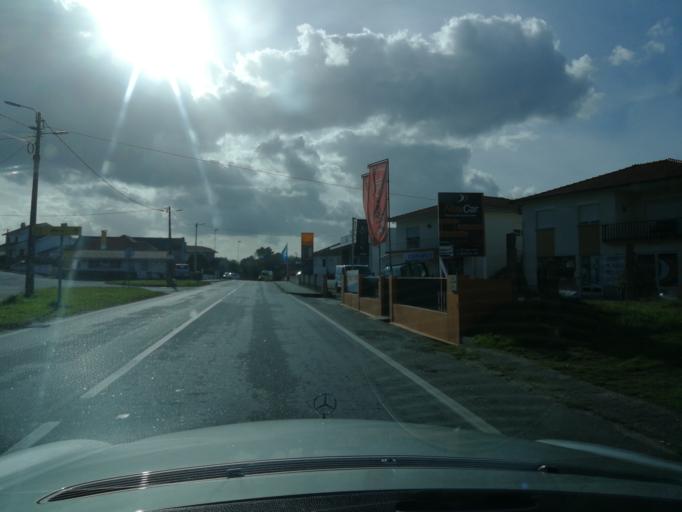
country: PT
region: Viana do Castelo
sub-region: Valenca
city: Valenza
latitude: 42.0292
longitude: -8.6324
